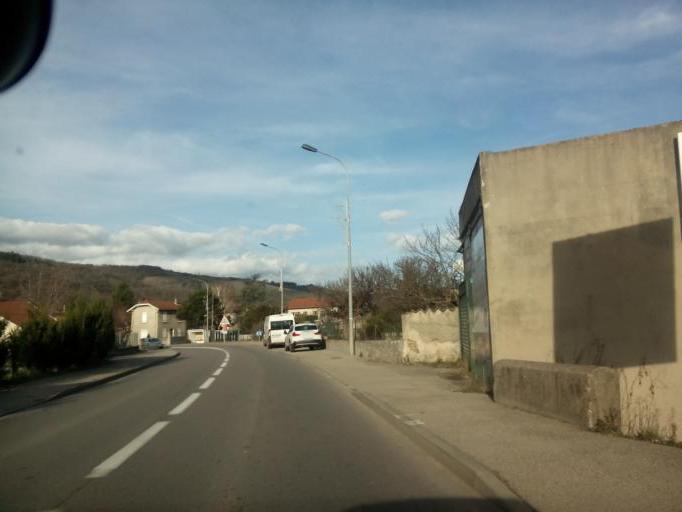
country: FR
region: Rhone-Alpes
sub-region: Departement de l'Isere
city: Sablons
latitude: 45.3192
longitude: 4.7710
